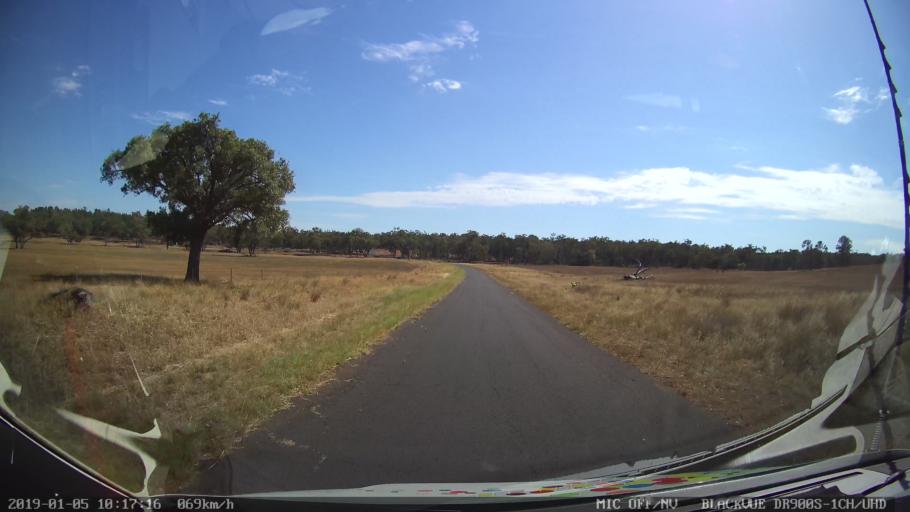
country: AU
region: New South Wales
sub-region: Gilgandra
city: Gilgandra
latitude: -31.5685
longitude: 148.9593
